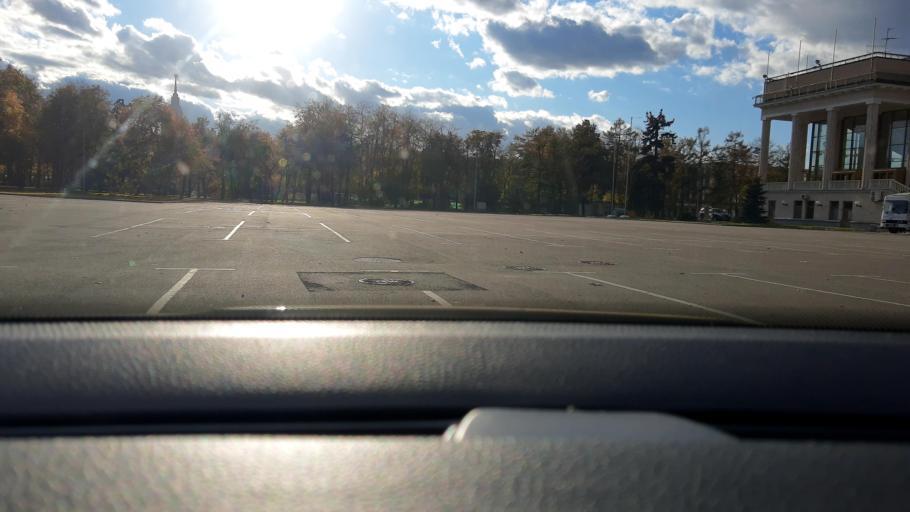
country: RU
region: Moscow
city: Luzhniki
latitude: 55.7177
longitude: 37.5512
